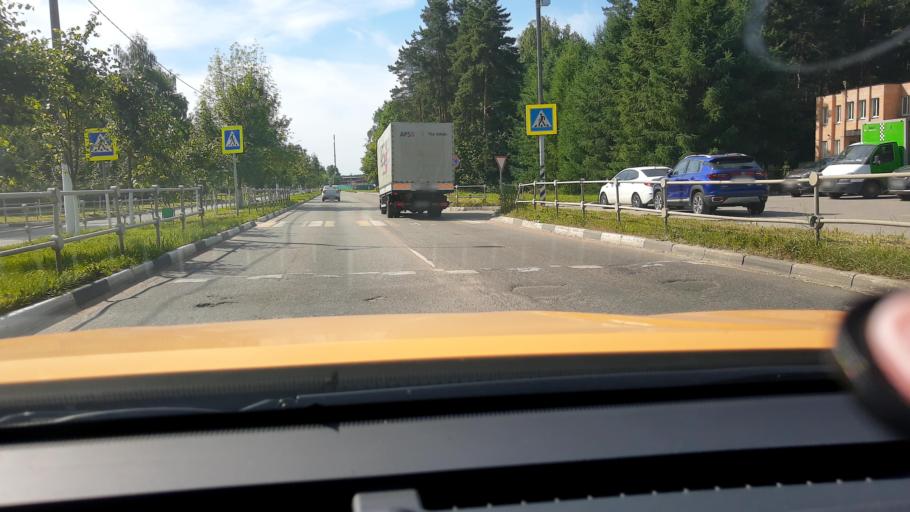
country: RU
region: Moskovskaya
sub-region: Podol'skiy Rayon
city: Podol'sk
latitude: 55.4148
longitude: 37.5216
